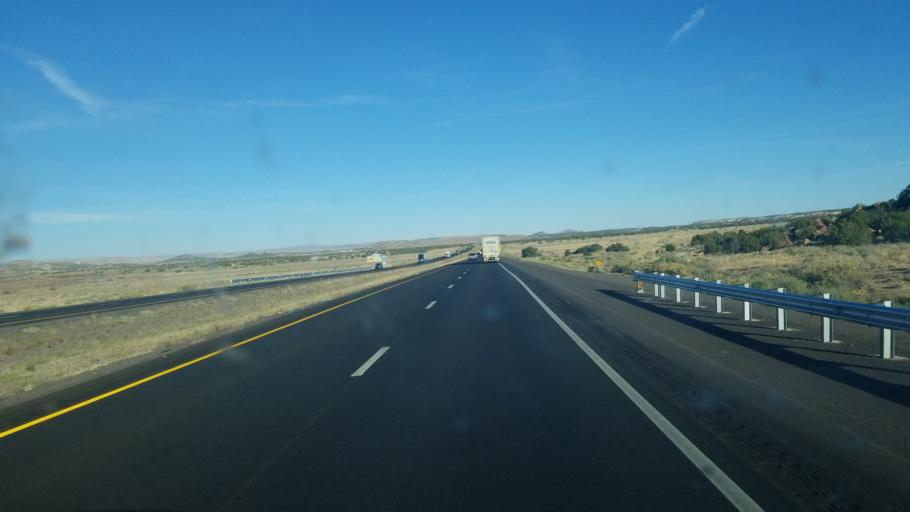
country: US
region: New Mexico
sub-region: Cibola County
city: Laguna
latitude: 35.0270
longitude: -107.4440
